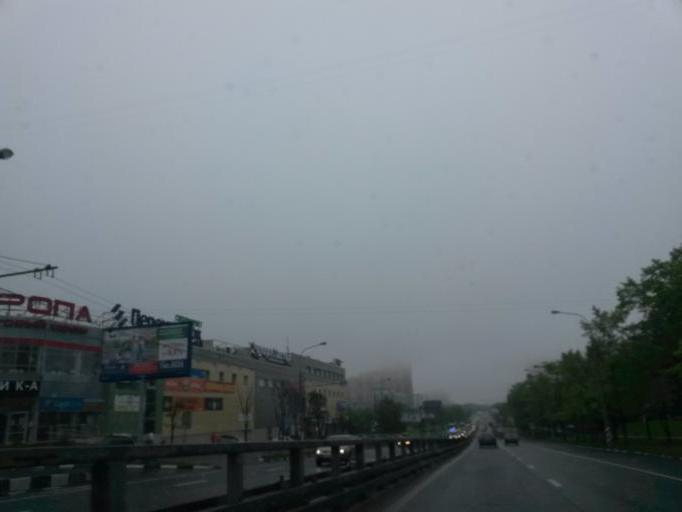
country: RU
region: Moscow
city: Yasenevo
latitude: 55.6353
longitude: 37.5213
